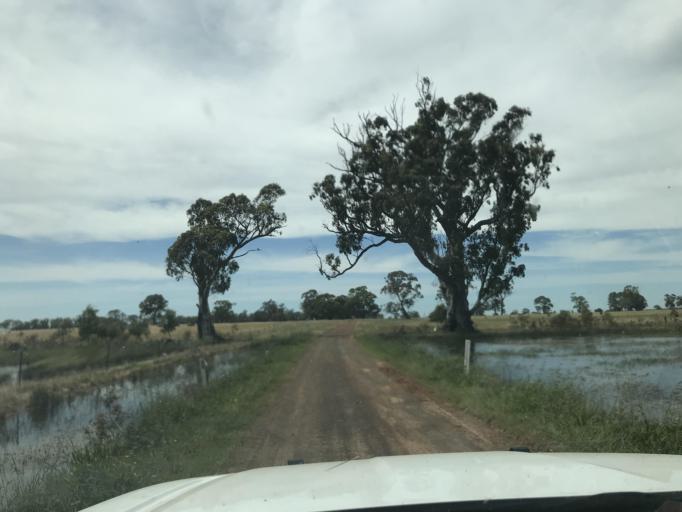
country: AU
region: South Australia
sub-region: Wattle Range
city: Penola
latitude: -37.0122
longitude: 141.4744
